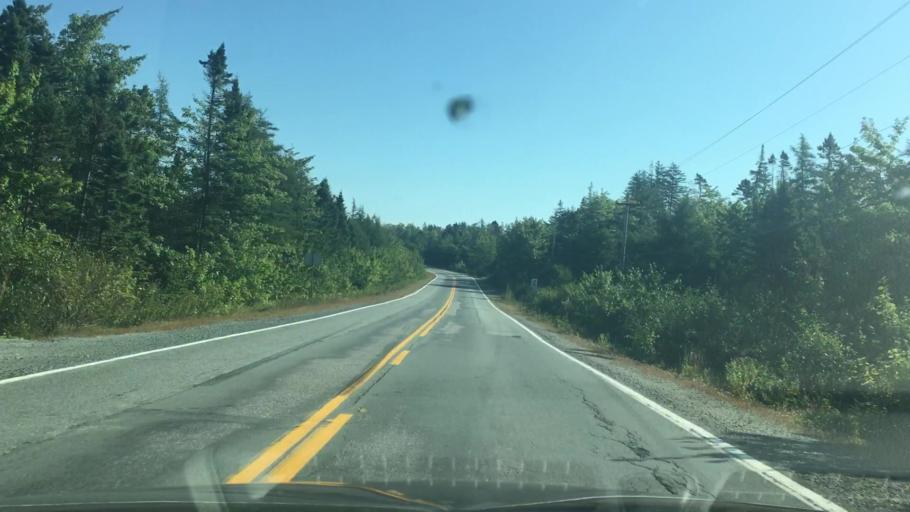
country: CA
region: Nova Scotia
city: Cole Harbour
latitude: 44.7752
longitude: -63.0510
